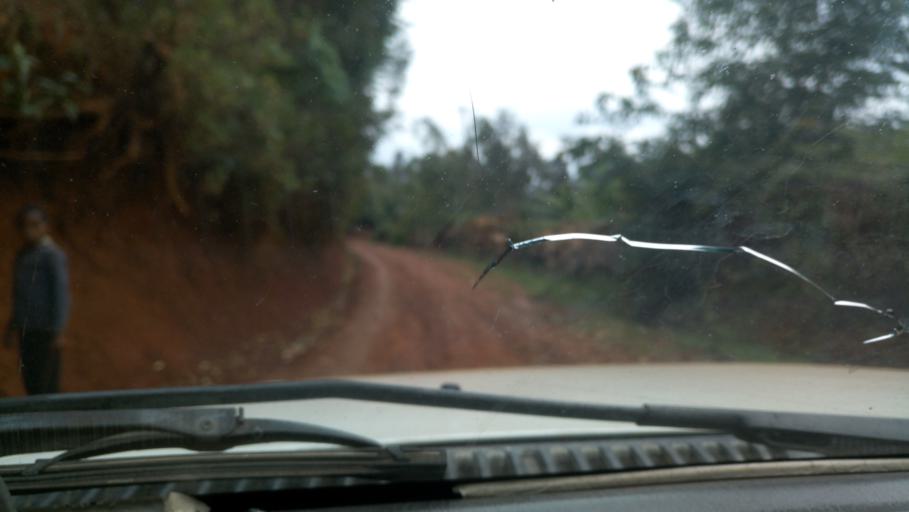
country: KE
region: Murang'a District
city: Kangema
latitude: -0.7950
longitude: 36.9621
